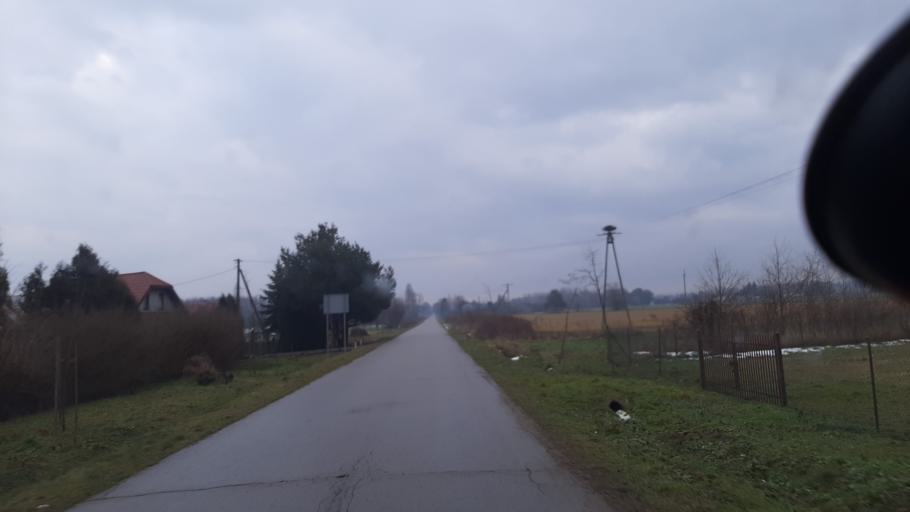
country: PL
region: Lublin Voivodeship
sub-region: Powiat lubelski
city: Lublin
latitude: 51.3391
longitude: 22.5396
